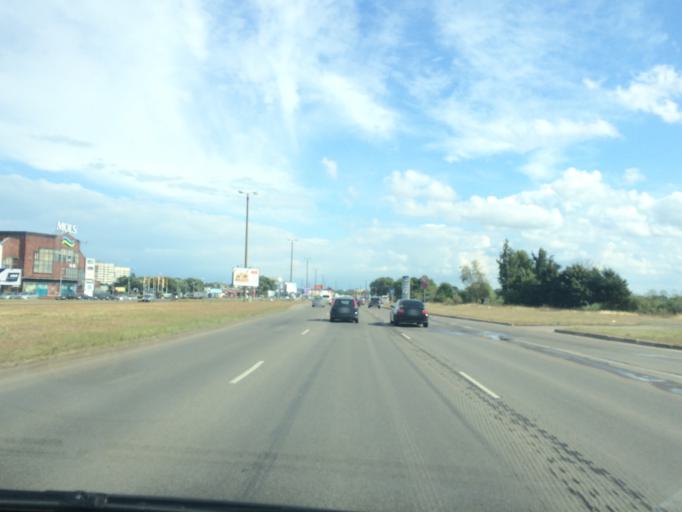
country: LV
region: Riga
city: Riga
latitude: 56.9344
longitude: 24.1395
